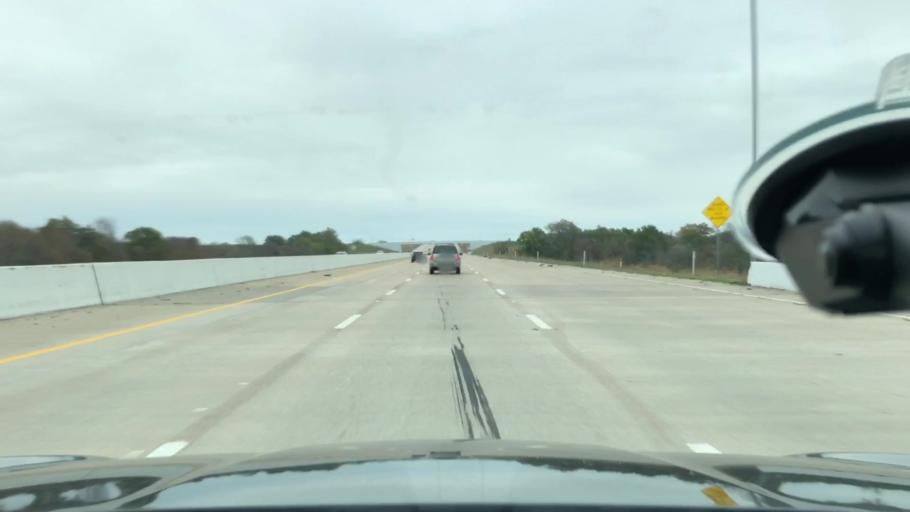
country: US
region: Texas
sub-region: Ellis County
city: Plum Grove
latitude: 32.1375
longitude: -96.9495
